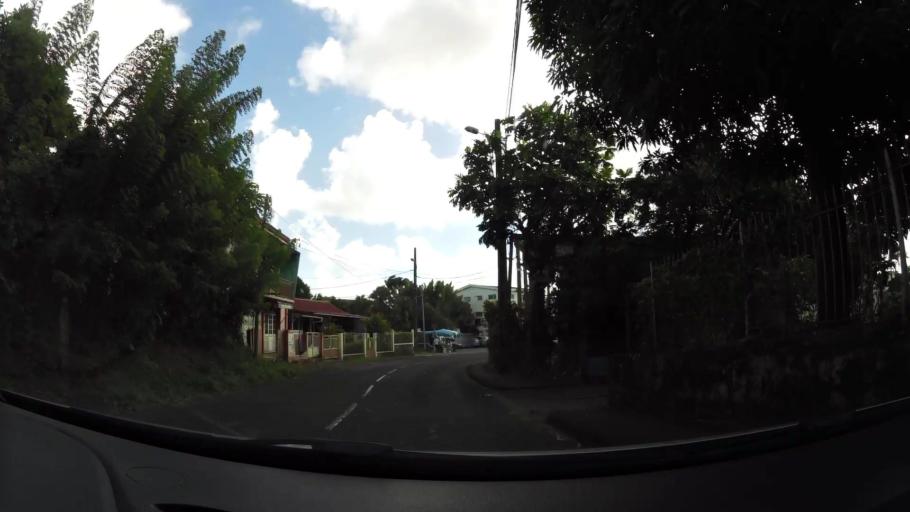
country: MQ
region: Martinique
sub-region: Martinique
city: Fort-de-France
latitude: 14.6248
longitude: -61.0608
